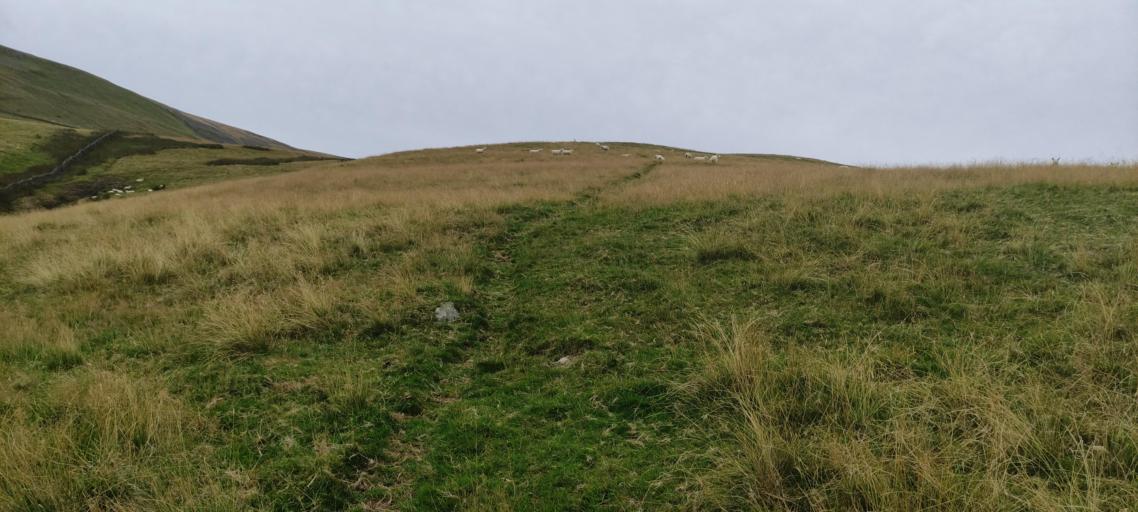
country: GB
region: England
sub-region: Cumbria
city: Appleby-in-Westmorland
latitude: 54.6832
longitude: -2.5195
